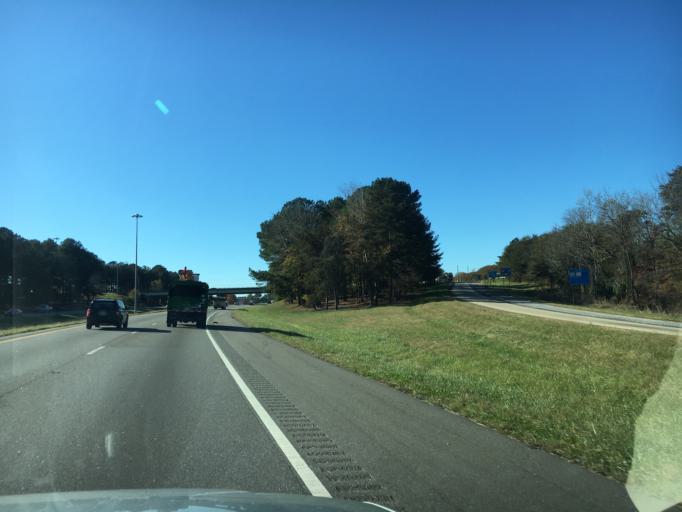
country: US
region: North Carolina
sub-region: Catawba County
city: Conover
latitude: 35.7031
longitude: -81.2585
